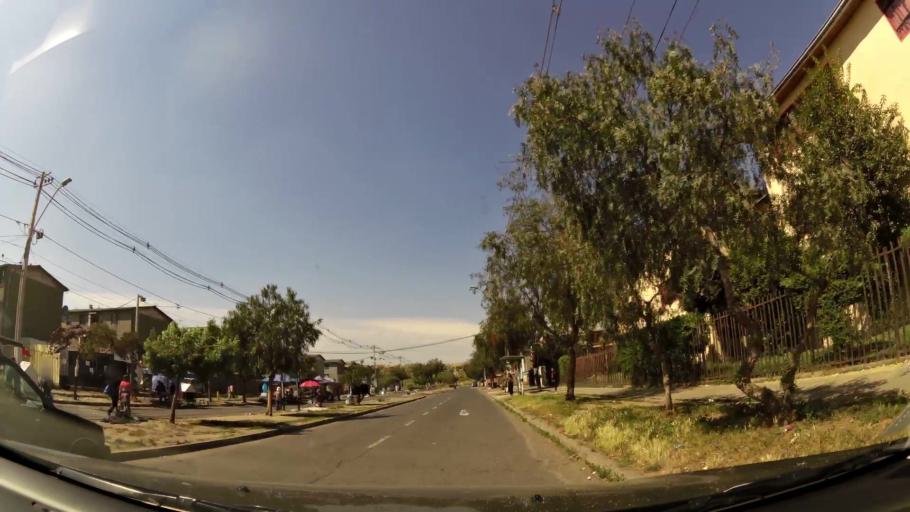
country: CL
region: Santiago Metropolitan
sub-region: Provincia de Cordillera
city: Puente Alto
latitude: -33.6204
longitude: -70.6042
